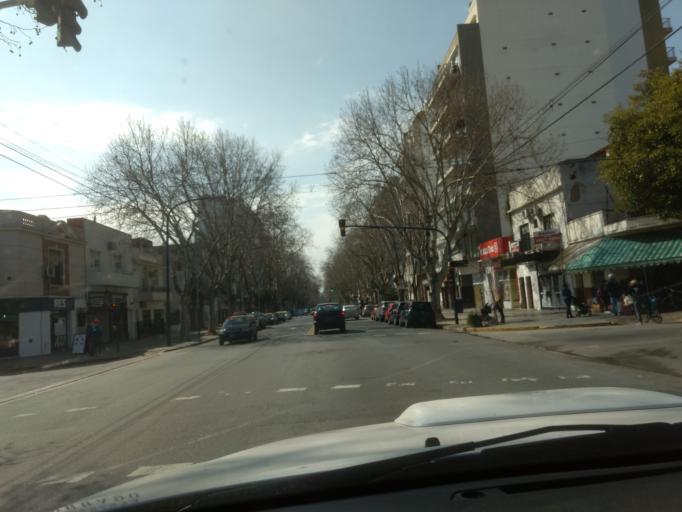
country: AR
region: Buenos Aires F.D.
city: Villa Santa Rita
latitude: -34.5875
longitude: -58.4827
